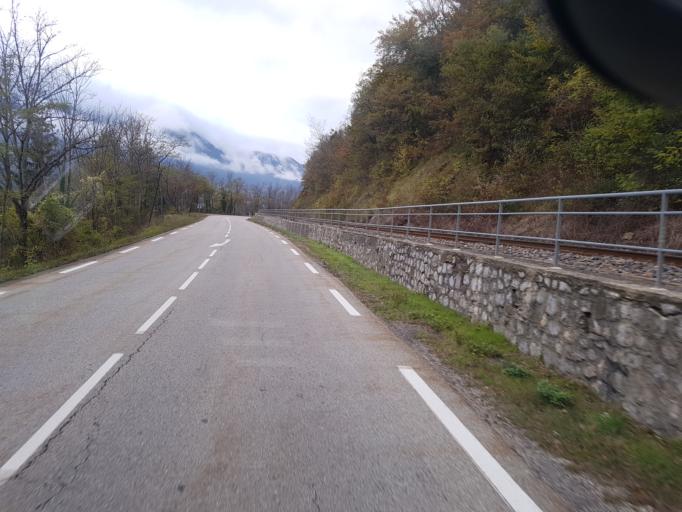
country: FR
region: Rhone-Alpes
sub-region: Departement de l'Isere
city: Le Gua
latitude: 44.9467
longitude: 5.6403
